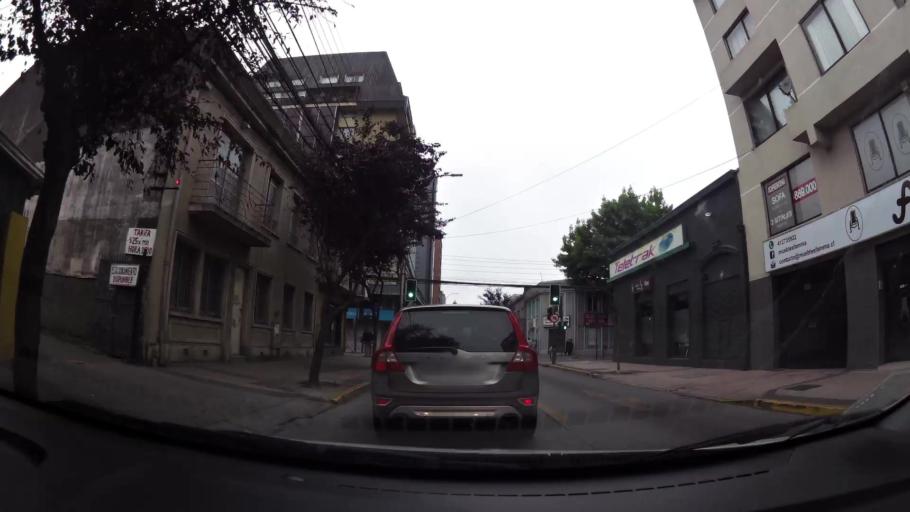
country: CL
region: Biobio
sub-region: Provincia de Concepcion
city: Concepcion
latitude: -36.8295
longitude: -73.0515
